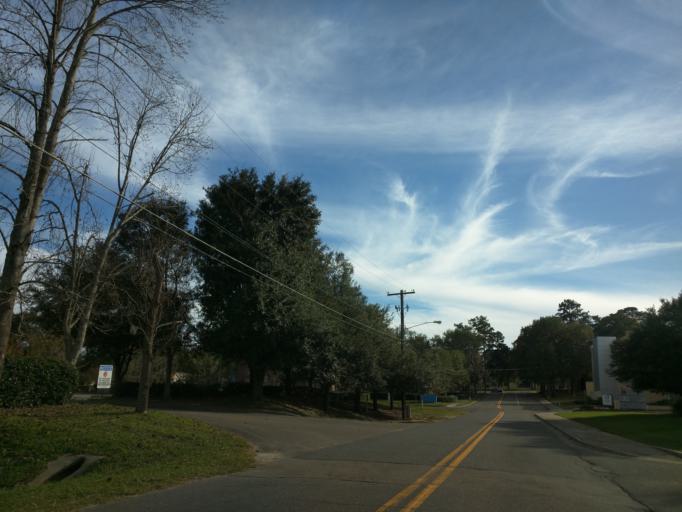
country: US
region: Florida
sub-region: Leon County
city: Tallahassee
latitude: 30.4573
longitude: -84.2411
